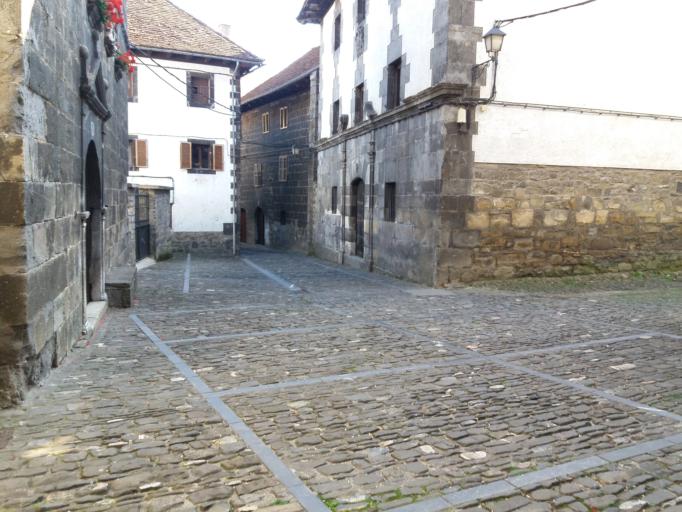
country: ES
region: Navarre
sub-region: Provincia de Navarra
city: Oronz
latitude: 42.9058
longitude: -1.0906
